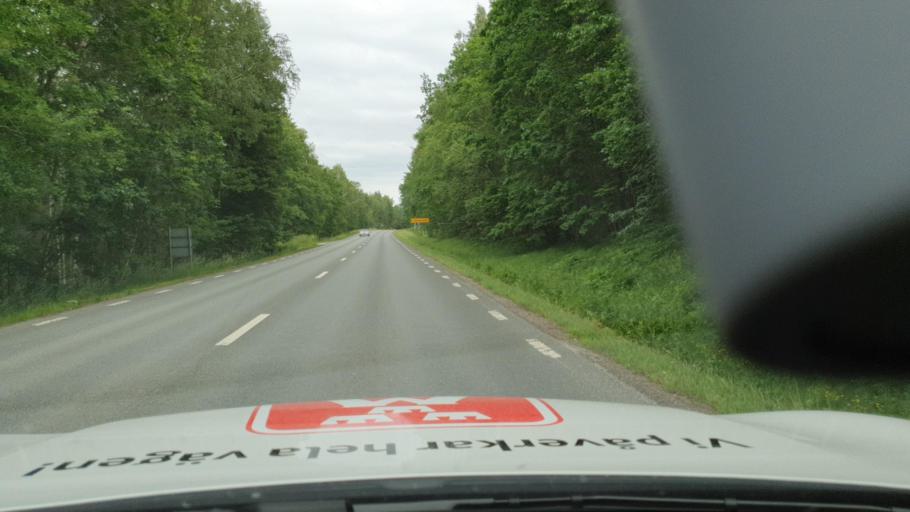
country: SE
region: Vaestra Goetaland
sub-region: Tidaholms Kommun
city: Tidaholm
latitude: 58.1882
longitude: 13.9963
